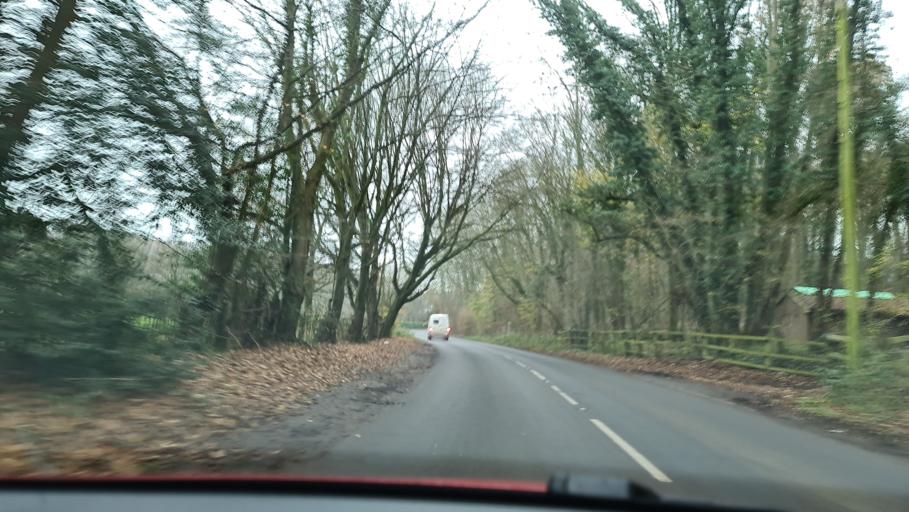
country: GB
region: England
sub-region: Buckinghamshire
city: Seer Green
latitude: 51.6084
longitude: -0.5980
